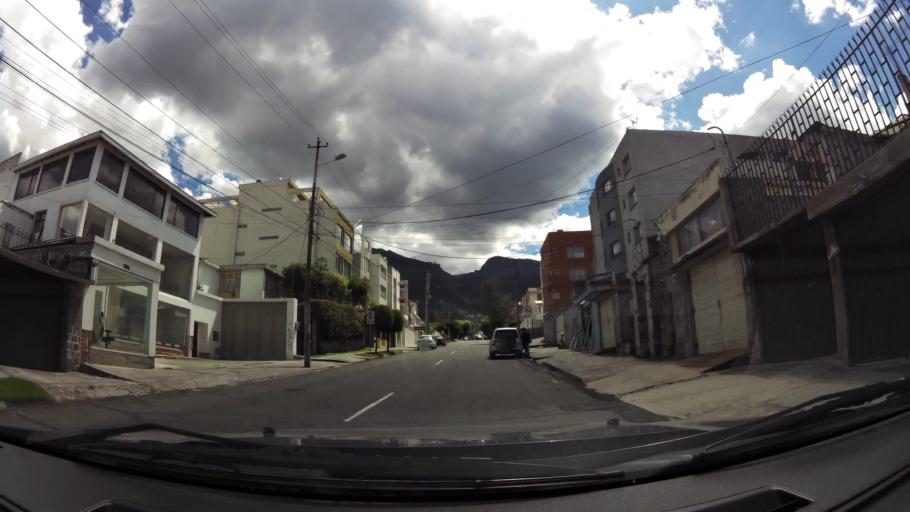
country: EC
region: Pichincha
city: Quito
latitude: -0.1911
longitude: -78.5010
